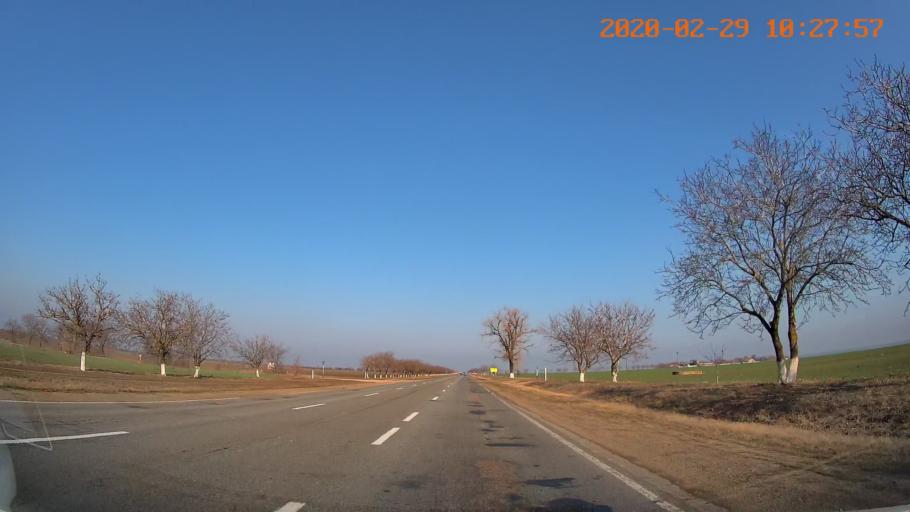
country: MD
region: Telenesti
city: Tiraspolul Nou
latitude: 46.9034
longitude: 29.5945
